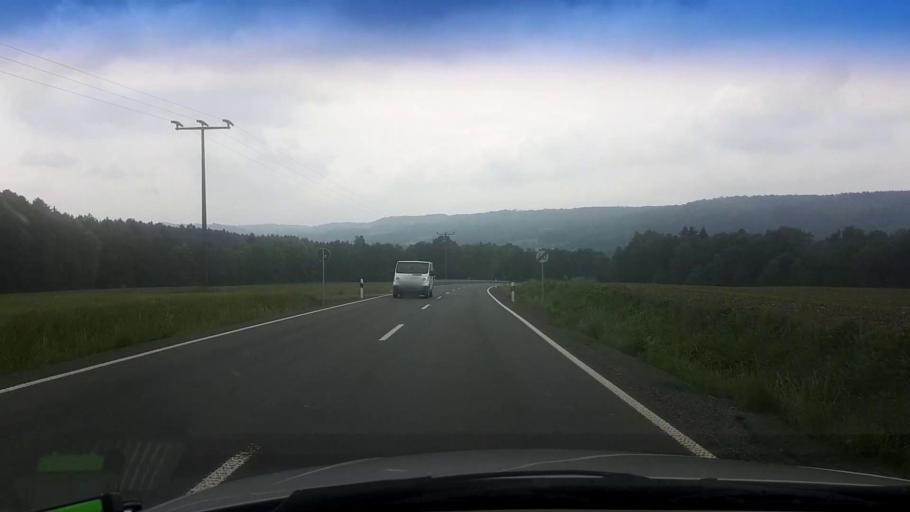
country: DE
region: Bavaria
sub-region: Upper Franconia
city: Reuth
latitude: 49.9783
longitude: 11.6959
